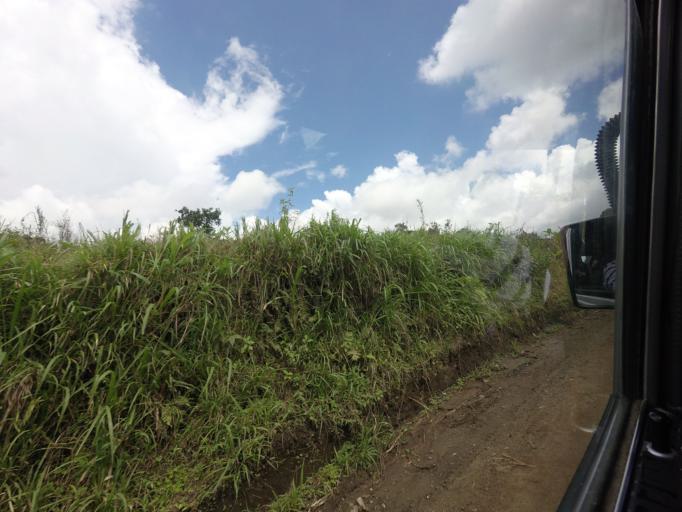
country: CO
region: Huila
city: Isnos
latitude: 1.9417
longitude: -76.2696
